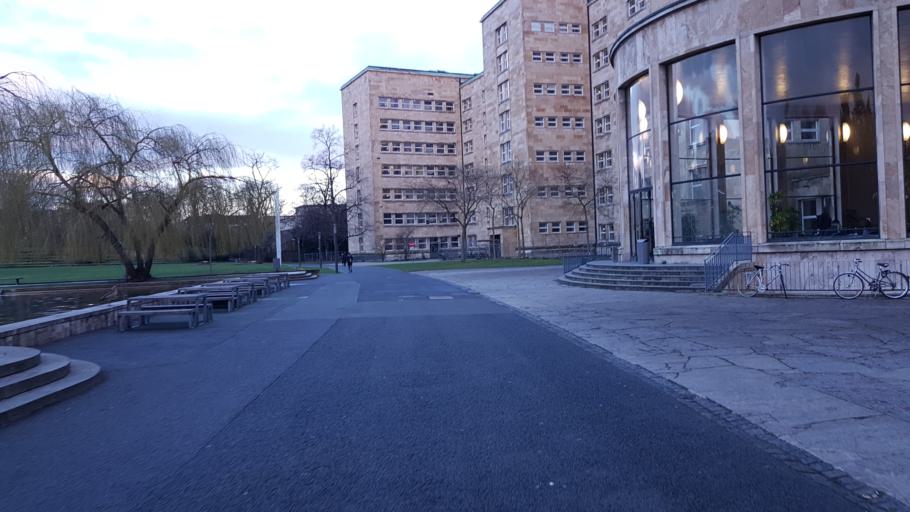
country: DE
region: Hesse
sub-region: Regierungsbezirk Darmstadt
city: Frankfurt am Main
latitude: 50.1257
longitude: 8.6670
